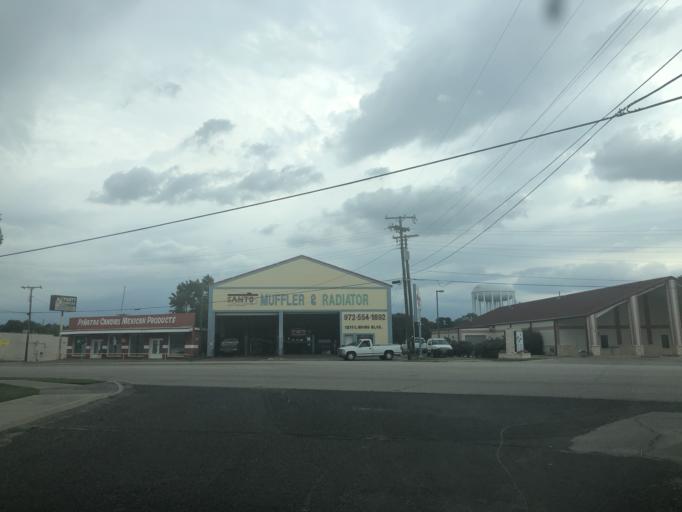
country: US
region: Texas
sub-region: Dallas County
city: Irving
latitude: 32.8100
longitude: -96.9318
